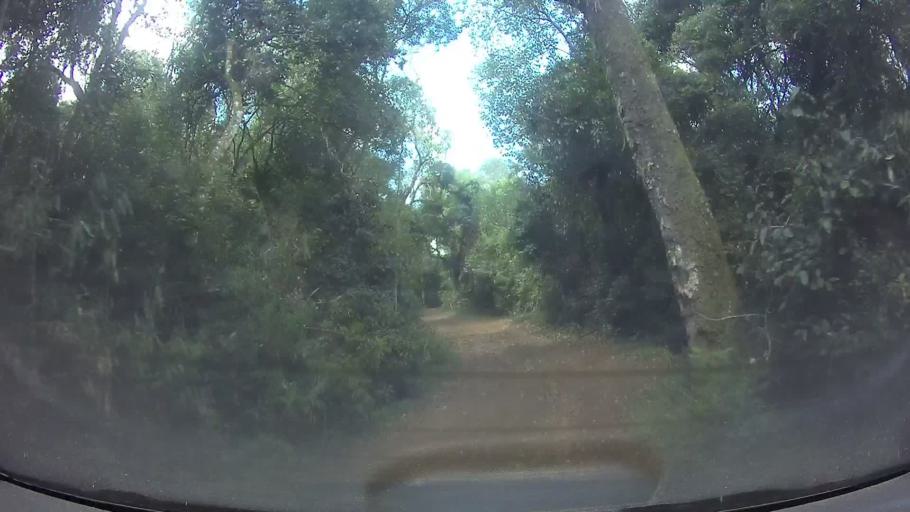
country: PY
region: Paraguari
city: La Colmena
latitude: -25.9760
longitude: -56.7291
